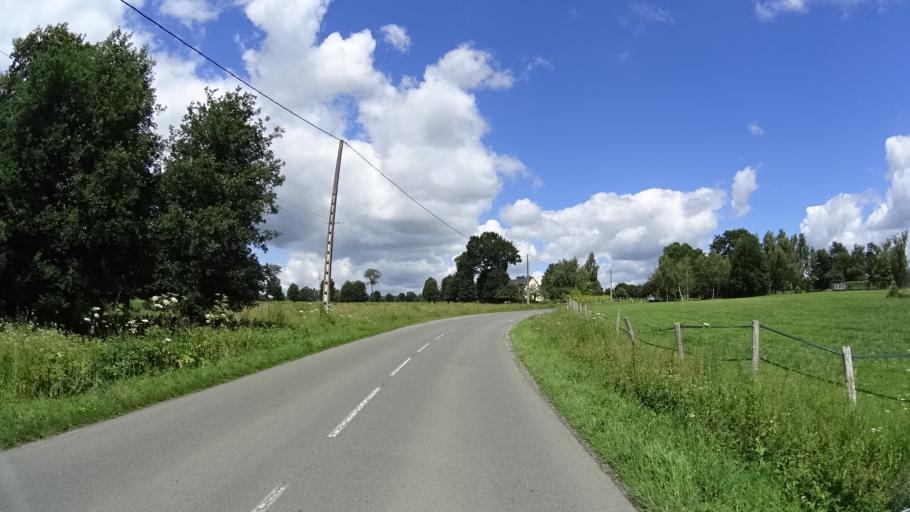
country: FR
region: Brittany
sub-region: Departement d'Ille-et-Vilaine
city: Saint-Gilles
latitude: 48.1375
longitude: -1.8271
